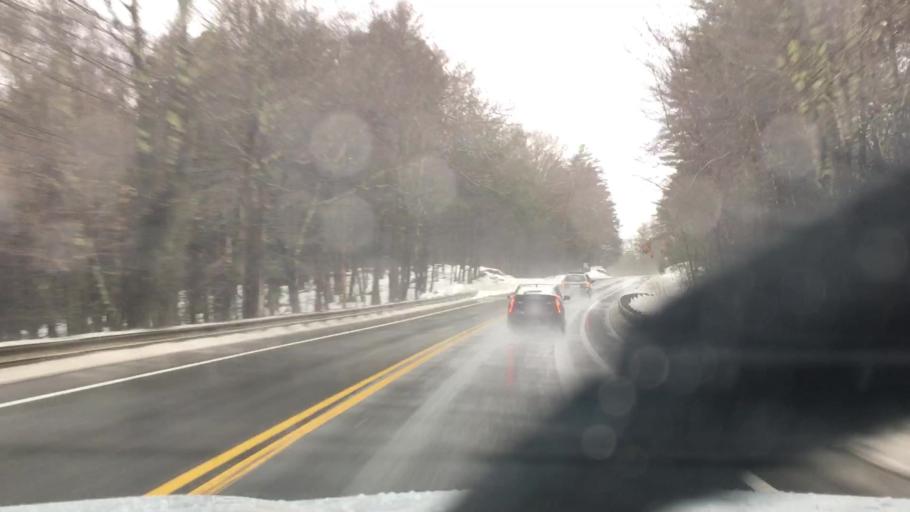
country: US
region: Massachusetts
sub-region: Franklin County
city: Shutesbury
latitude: 42.4390
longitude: -72.3894
